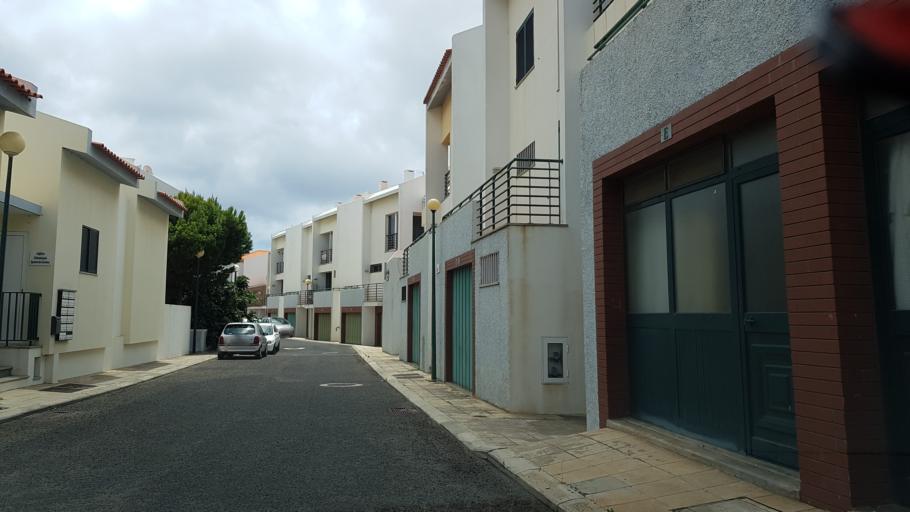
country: PT
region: Madeira
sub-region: Porto Santo
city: Vila de Porto Santo
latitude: 33.0639
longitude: -16.3361
